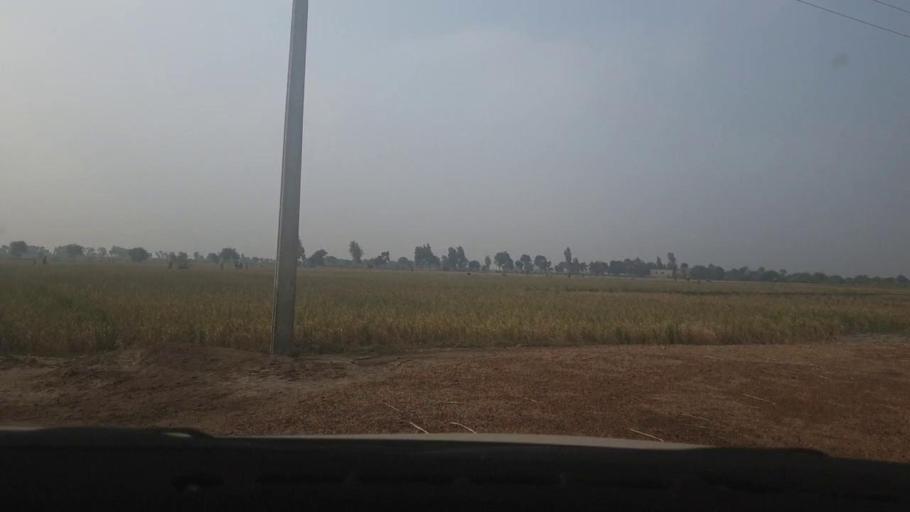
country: PK
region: Sindh
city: Tando Muhammad Khan
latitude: 25.1081
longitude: 68.5423
